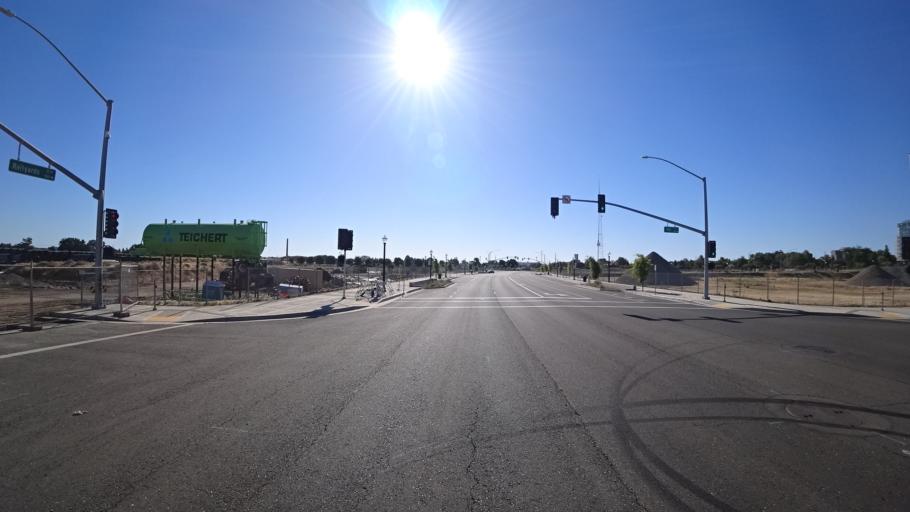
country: US
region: California
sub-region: Sacramento County
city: Sacramento
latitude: 38.5902
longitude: -121.4976
